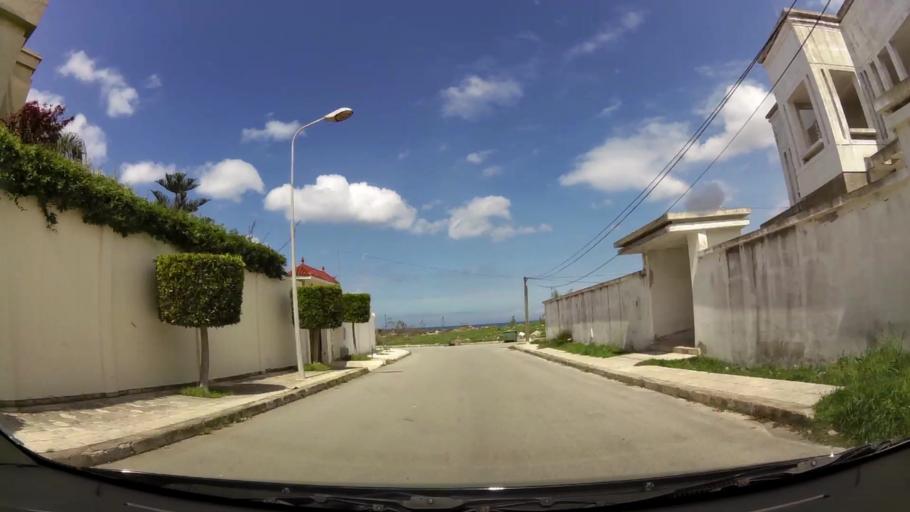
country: MA
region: Tanger-Tetouan
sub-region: Tanger-Assilah
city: Tangier
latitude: 35.7730
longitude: -5.7671
